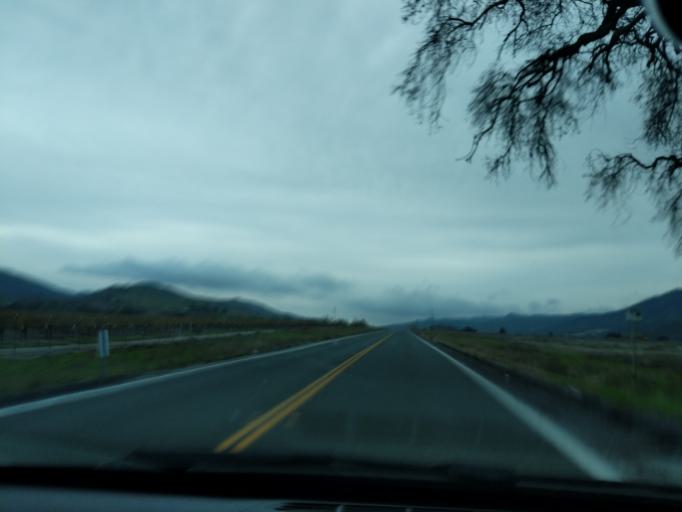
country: US
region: California
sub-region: San Benito County
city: Ridgemark
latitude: 36.6726
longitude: -121.2524
